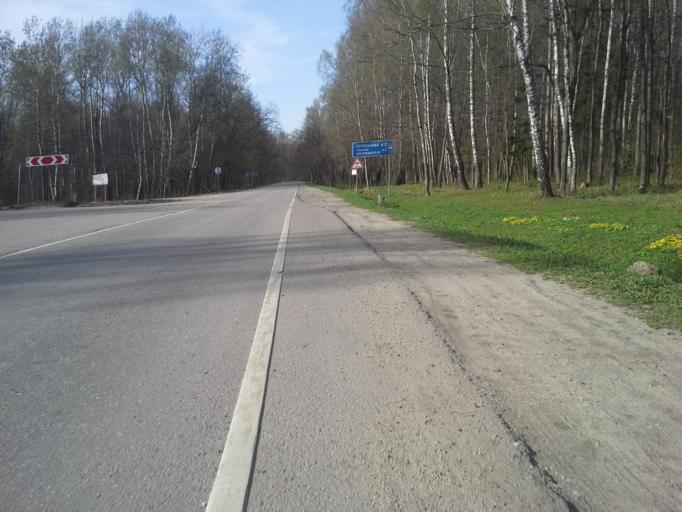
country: RU
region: Moskovskaya
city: Dubrovitsy
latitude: 55.4256
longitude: 37.3984
